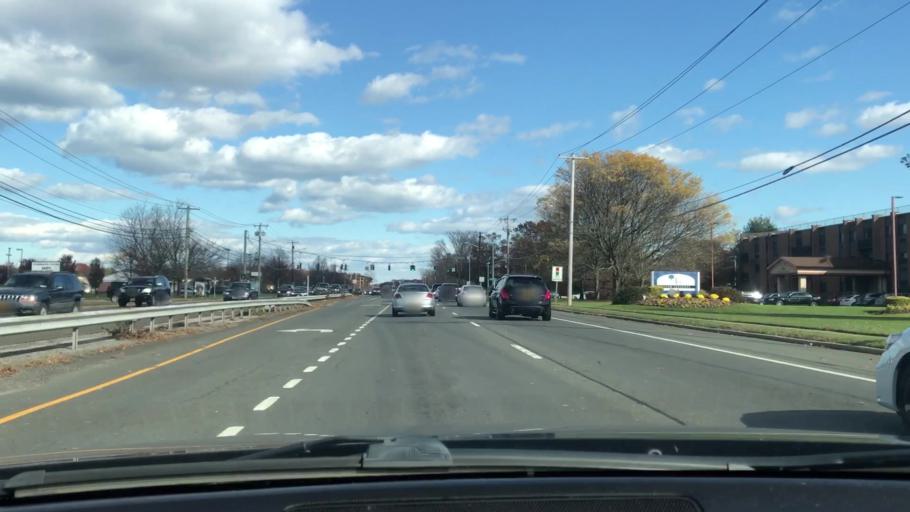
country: US
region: New York
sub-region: Suffolk County
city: Terryville
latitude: 40.9035
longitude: -73.0738
